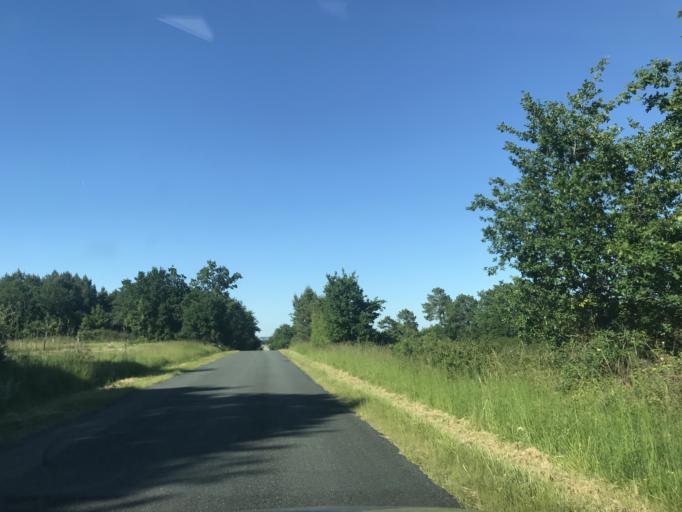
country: FR
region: Poitou-Charentes
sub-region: Departement de la Charente
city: Chalais
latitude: 45.2377
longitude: -0.0068
